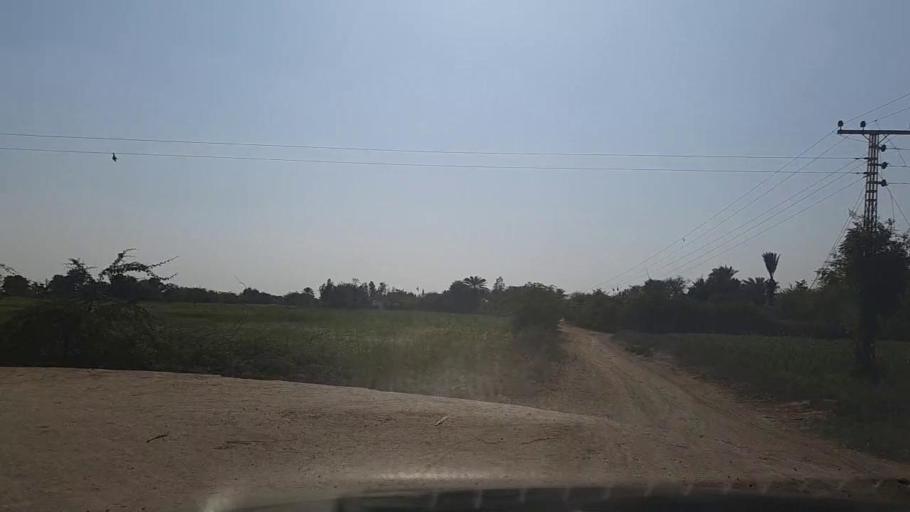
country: PK
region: Sindh
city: Digri
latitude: 25.1395
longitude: 69.1155
